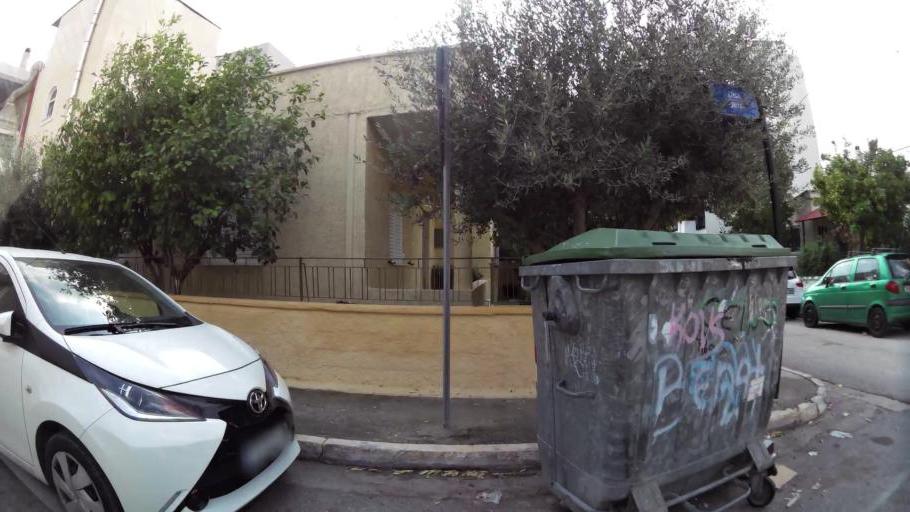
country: GR
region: Attica
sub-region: Nomarchia Athinas
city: Ilion
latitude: 38.0405
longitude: 23.7001
